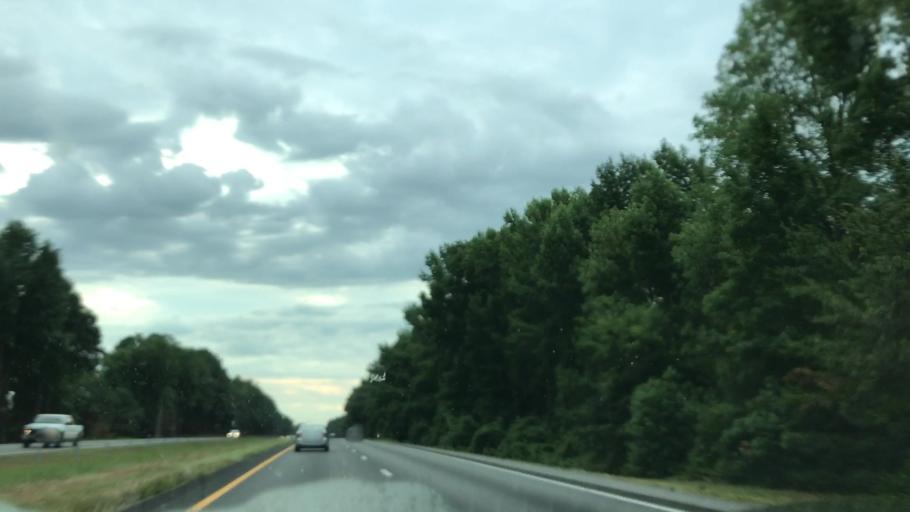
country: US
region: North Carolina
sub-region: Johnston County
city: Four Oaks
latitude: 35.4221
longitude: -78.4501
